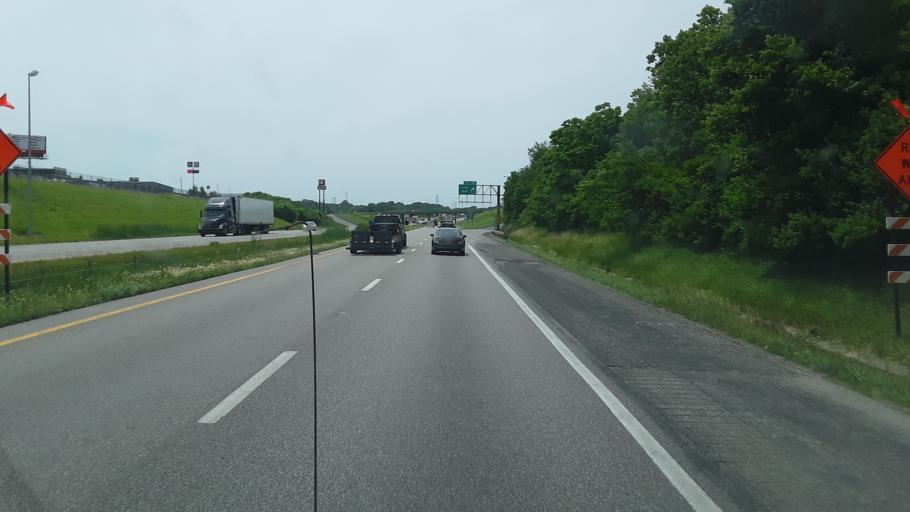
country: US
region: Missouri
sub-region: Saint Louis County
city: Glasgow Village
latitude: 38.7675
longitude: -90.1975
